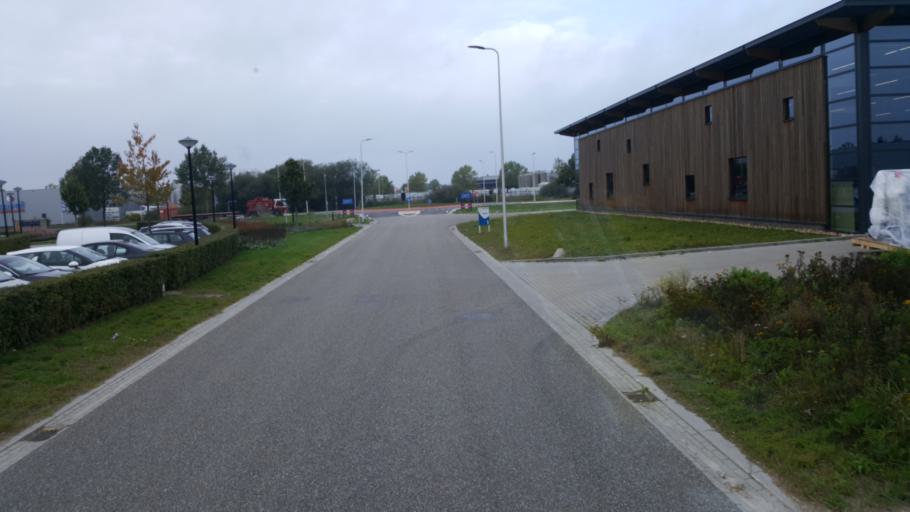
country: NL
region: Overijssel
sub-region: Gemeente Wierden
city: Wierden
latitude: 52.3565
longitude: 6.5102
